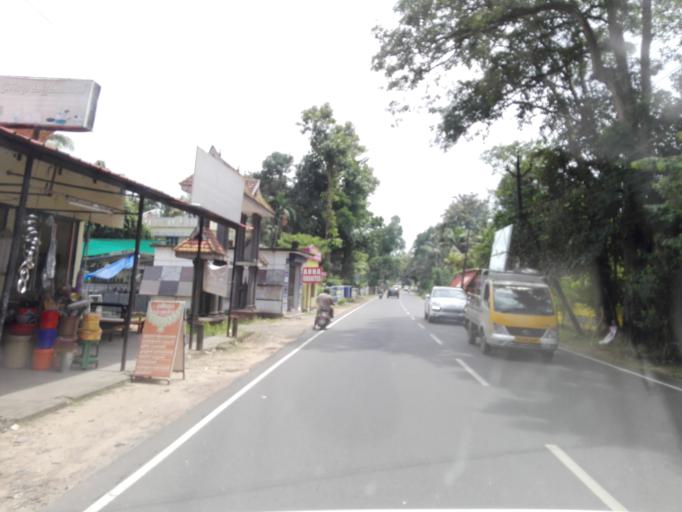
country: IN
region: Kerala
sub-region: Alappuzha
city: Arukutti
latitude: 9.8586
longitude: 76.3831
